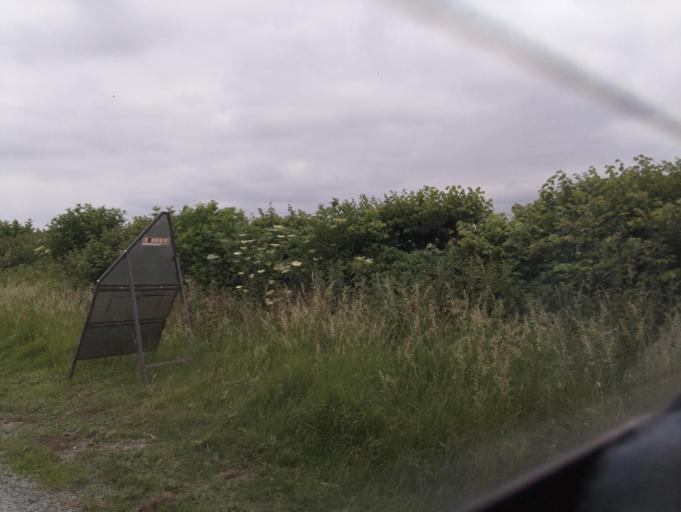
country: GB
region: England
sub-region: District of Rutland
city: Exton
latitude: 52.6707
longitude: -0.6438
